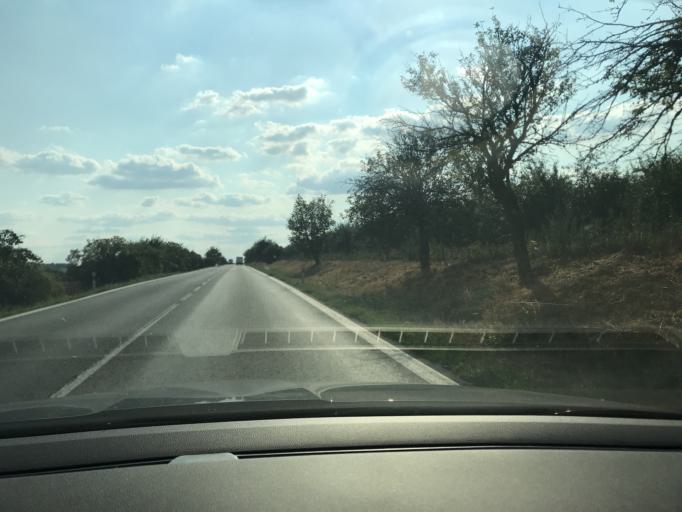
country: CZ
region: Central Bohemia
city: Brandysek
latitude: 50.2587
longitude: 14.1700
